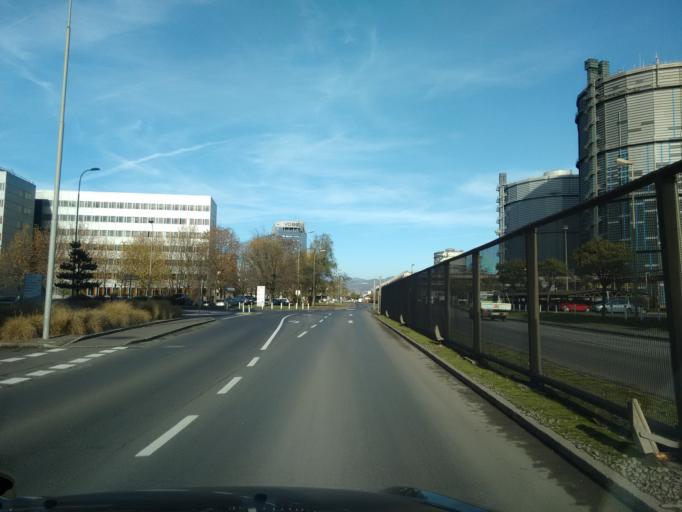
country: AT
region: Upper Austria
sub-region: Politischer Bezirk Urfahr-Umgebung
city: Steyregg
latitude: 48.2748
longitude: 14.3230
